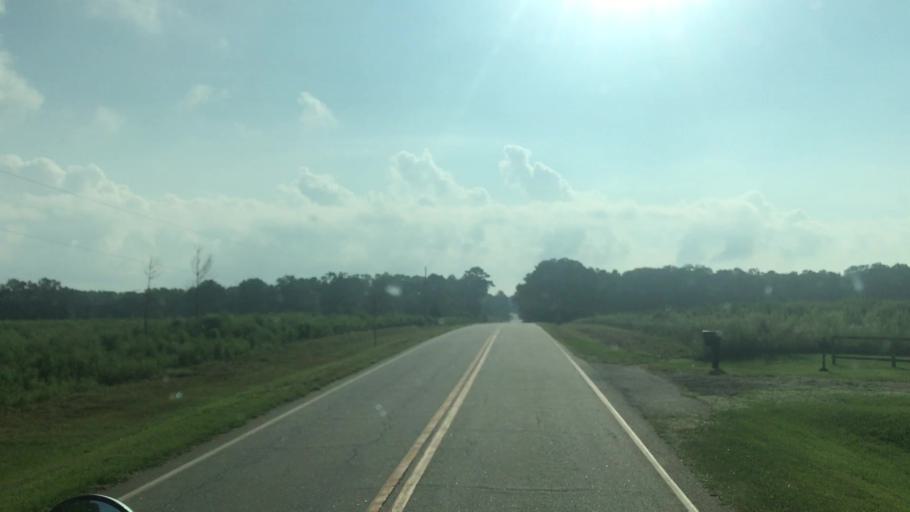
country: US
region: Florida
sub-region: Gadsden County
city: Quincy
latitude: 30.6983
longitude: -84.5330
